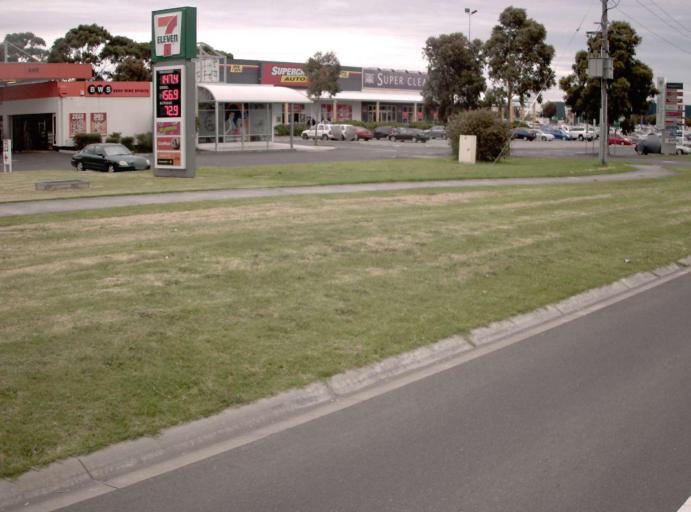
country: AU
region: Victoria
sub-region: Casey
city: Cranbourne North
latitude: -38.0808
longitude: 145.2757
